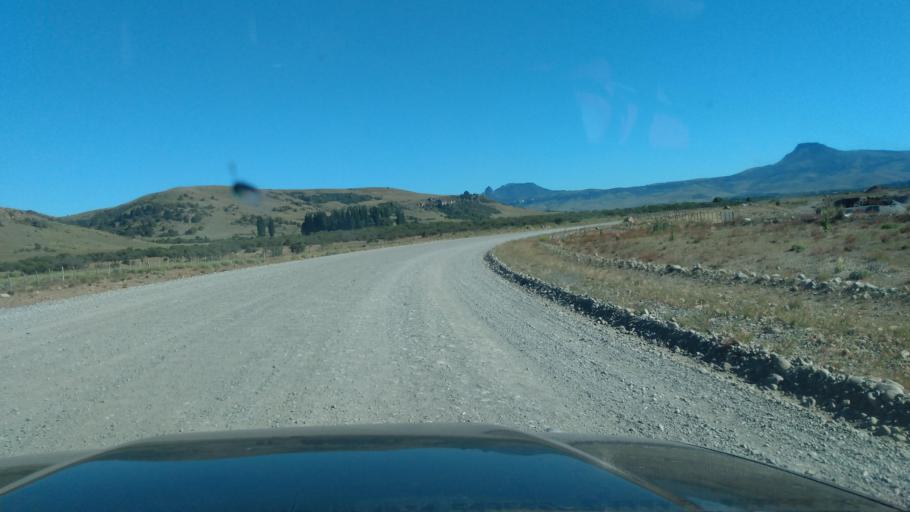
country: AR
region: Neuquen
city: Junin de los Andes
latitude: -39.8569
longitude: -71.1882
